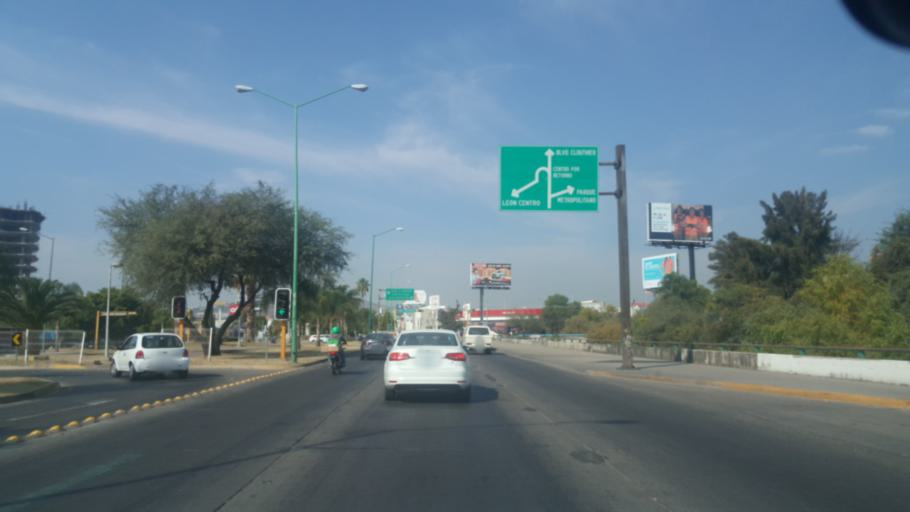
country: MX
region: Guanajuato
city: Leon
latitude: 21.1546
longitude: -101.6829
